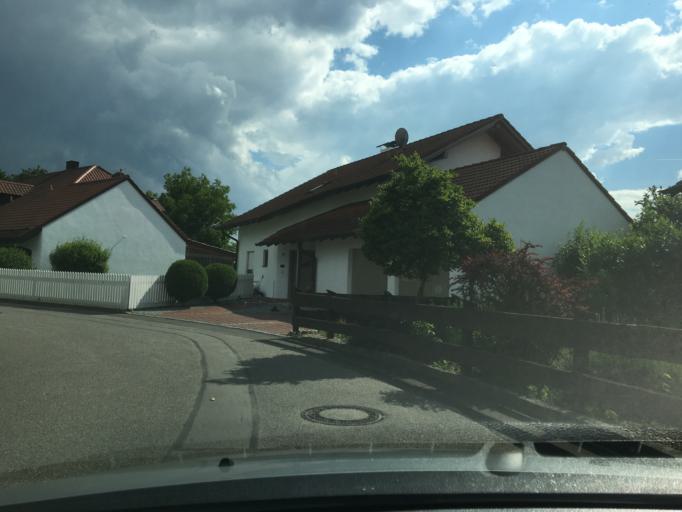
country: DE
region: Bavaria
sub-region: Lower Bavaria
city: Eching
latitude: 48.4937
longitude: 12.0260
